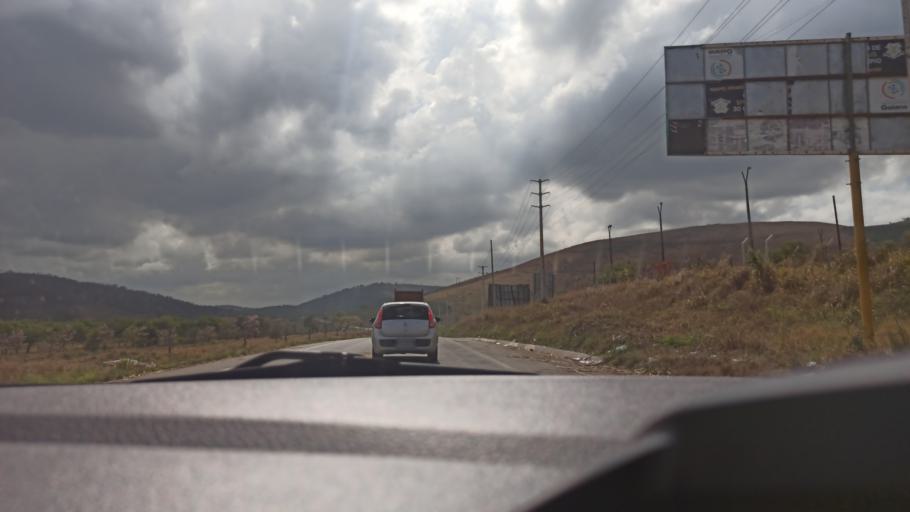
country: BR
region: Pernambuco
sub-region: Timbauba
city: Timbauba
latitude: -7.5215
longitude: -35.3032
